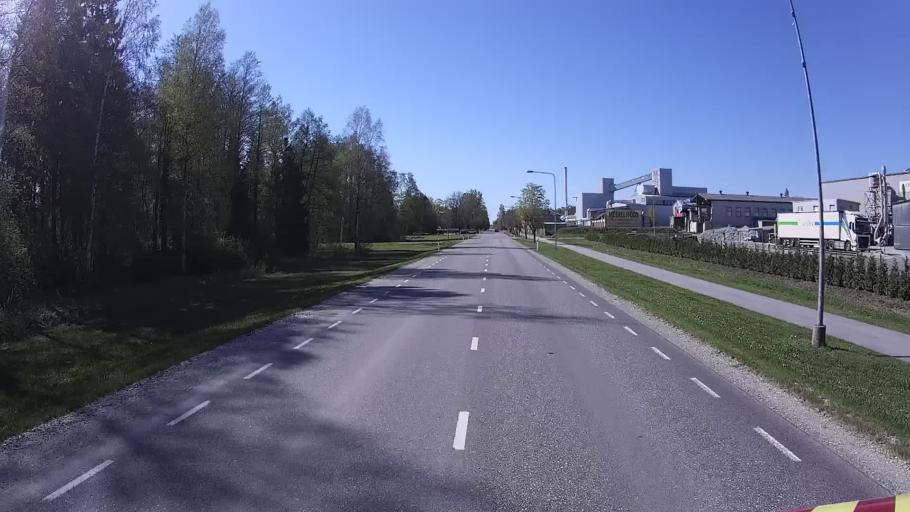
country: EE
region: Raplamaa
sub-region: Jaervakandi vald
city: Jarvakandi
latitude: 58.7807
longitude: 24.8174
